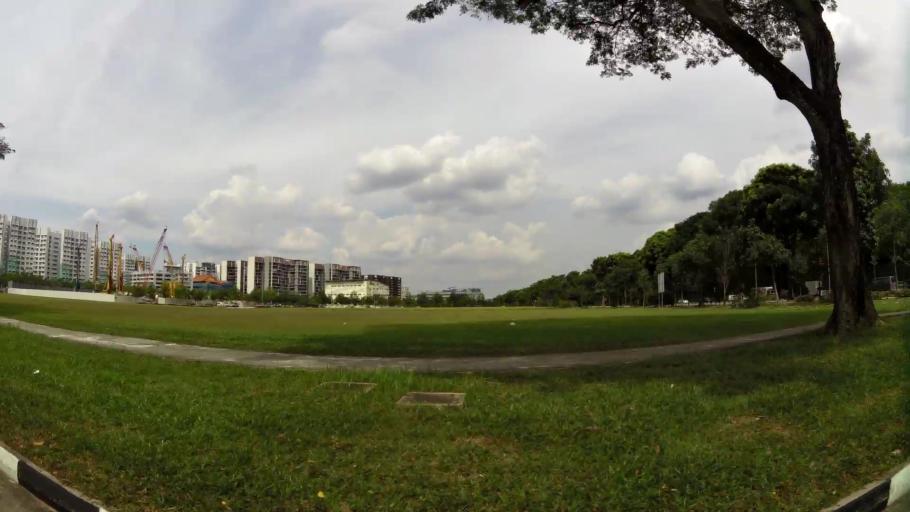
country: MY
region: Johor
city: Johor Bahru
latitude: 1.4272
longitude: 103.7985
